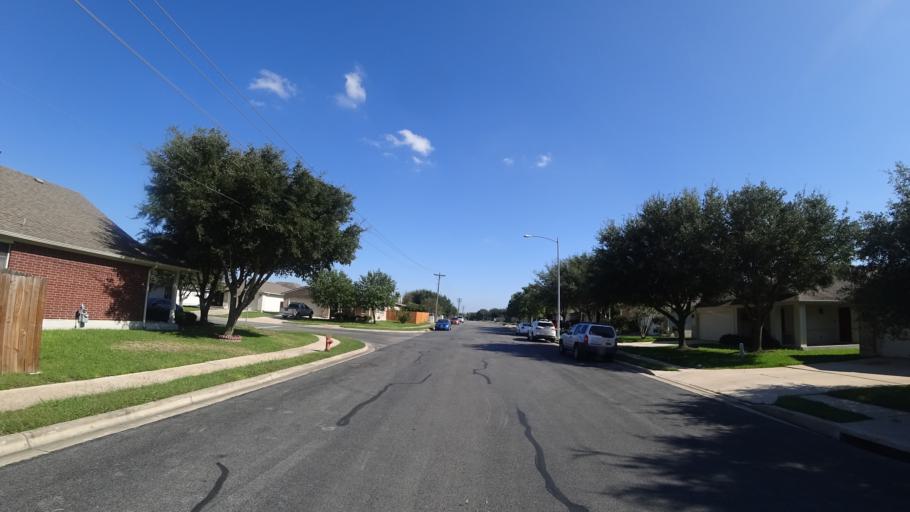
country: US
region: Texas
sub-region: Travis County
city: Manor
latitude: 30.3641
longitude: -97.6115
